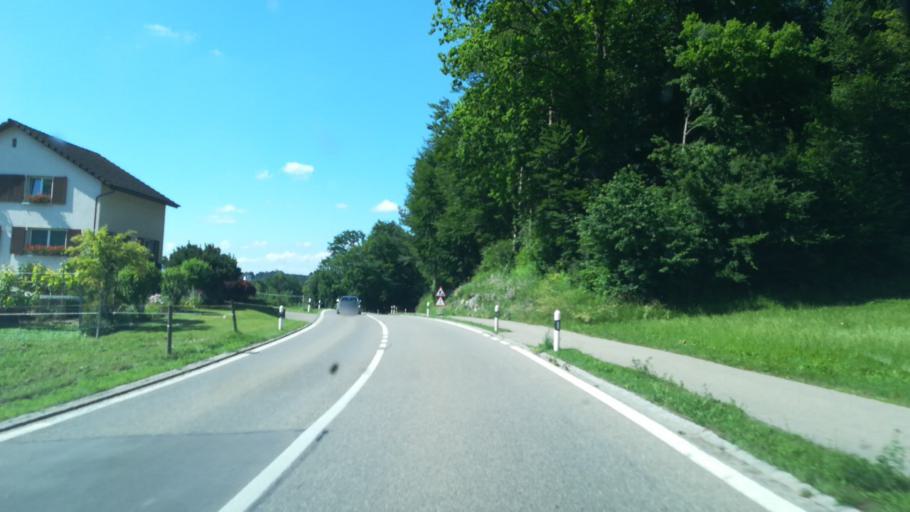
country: CH
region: Thurgau
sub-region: Weinfelden District
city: Sulgen
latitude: 47.5126
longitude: 9.2103
